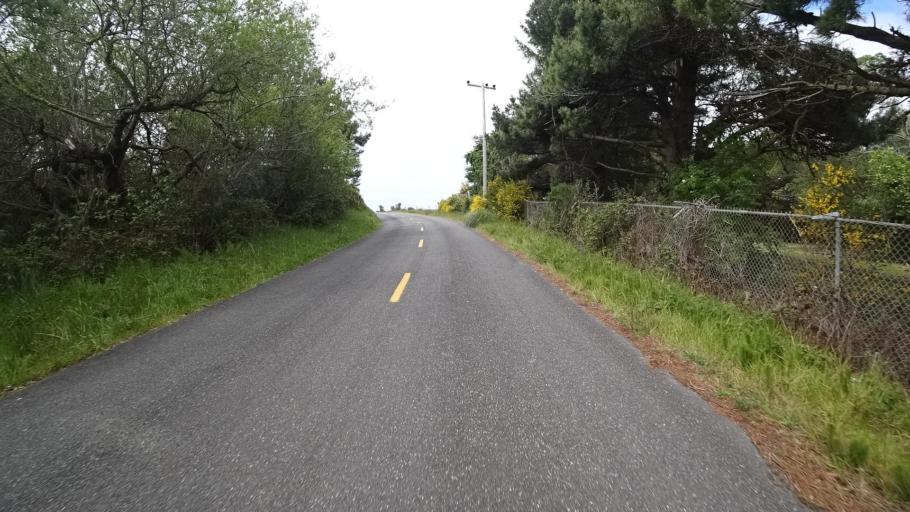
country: US
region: California
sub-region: Humboldt County
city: Humboldt Hill
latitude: 40.6867
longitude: -124.2400
